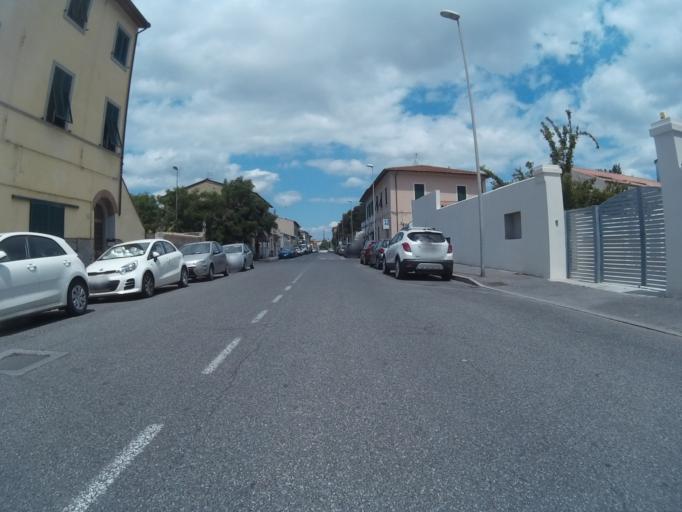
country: IT
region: Tuscany
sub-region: Provincia di Livorno
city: Livorno
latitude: 43.5647
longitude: 10.3309
